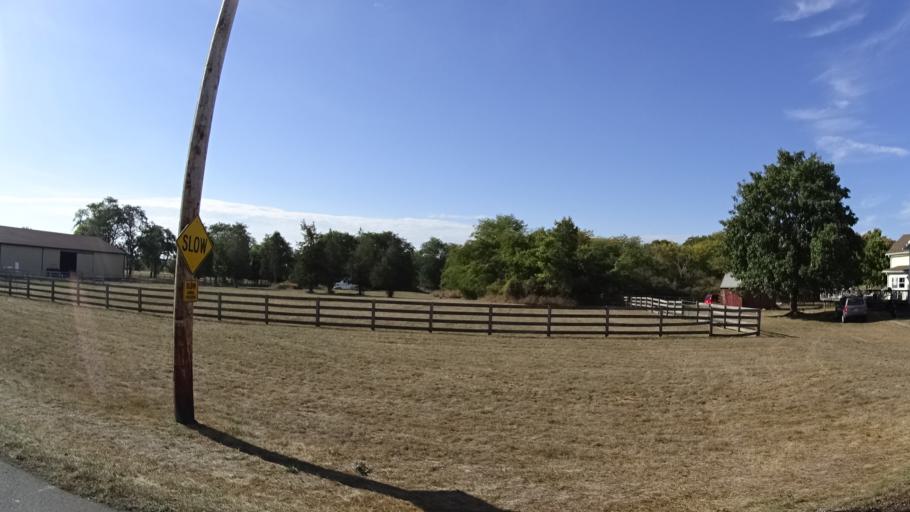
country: US
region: Ohio
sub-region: Erie County
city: Sandusky
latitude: 41.5960
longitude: -82.7002
